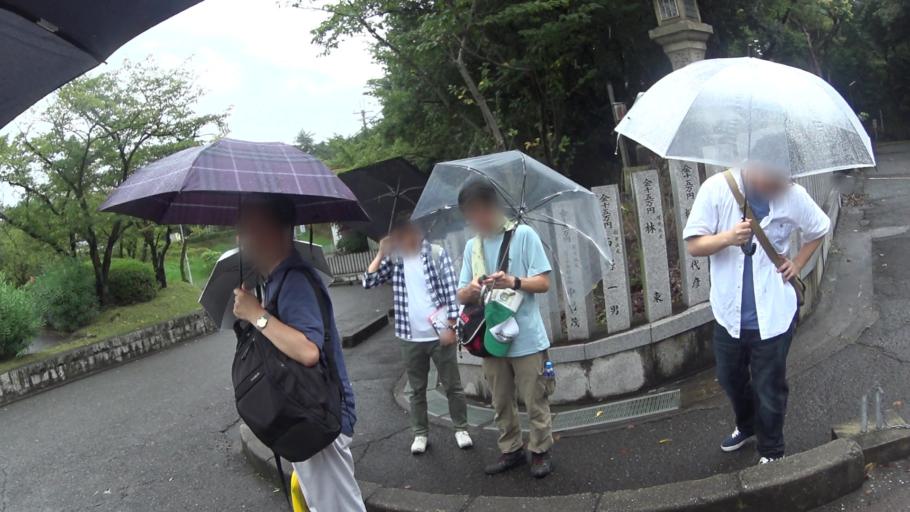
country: JP
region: Osaka
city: Takaishi
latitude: 34.5029
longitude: 135.4981
